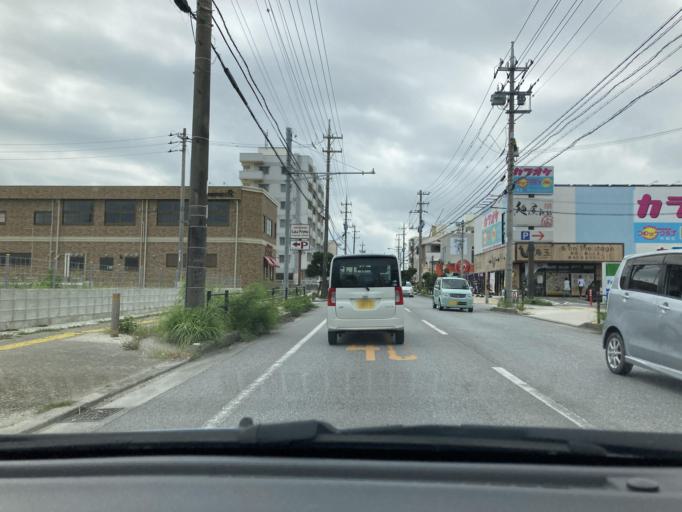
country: JP
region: Okinawa
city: Ginowan
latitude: 26.2448
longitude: 127.7688
